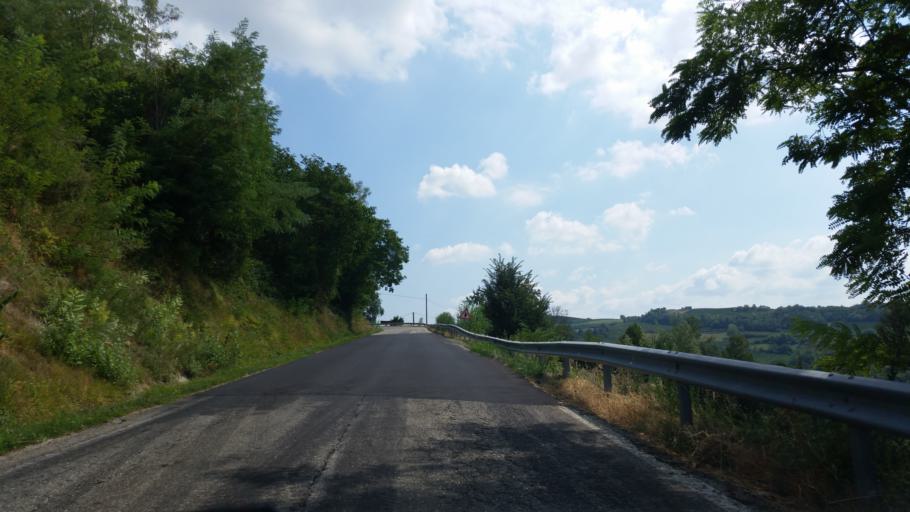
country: IT
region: Piedmont
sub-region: Provincia di Cuneo
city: Mango
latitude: 44.6929
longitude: 8.1401
